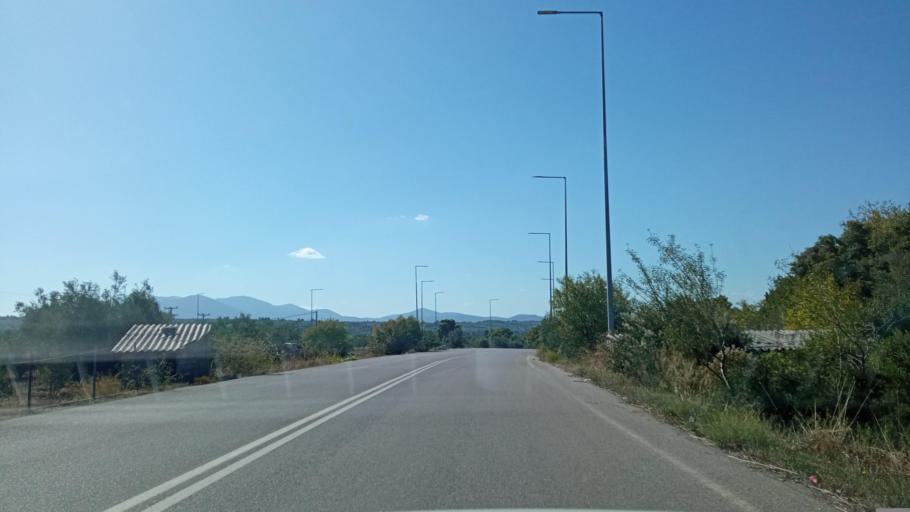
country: GR
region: Central Greece
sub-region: Nomos Evvoias
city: Psachna
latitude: 38.6000
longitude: 23.7481
